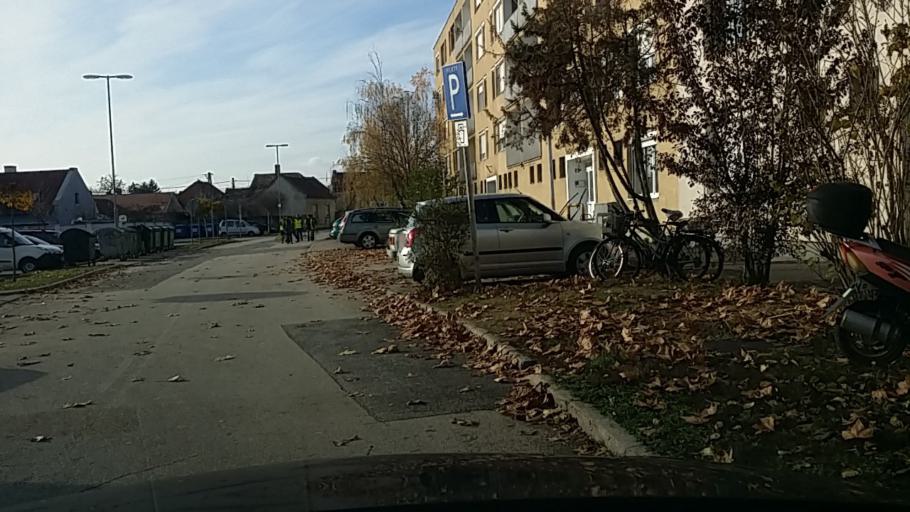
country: HU
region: Veszprem
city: Tapolca
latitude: 46.8818
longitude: 17.4388
